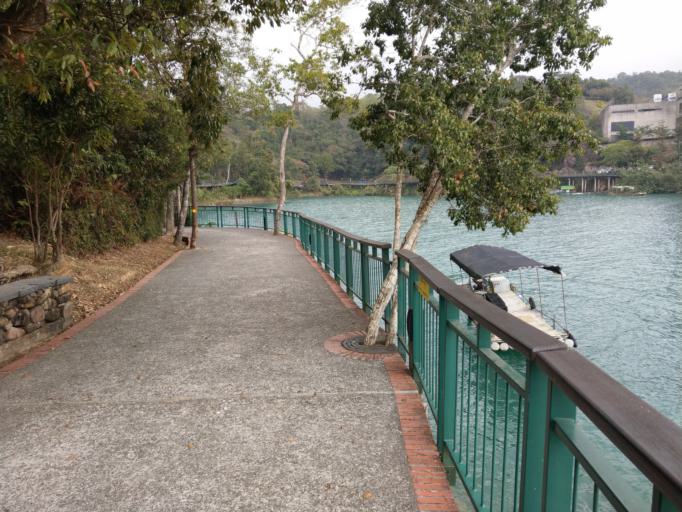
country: TW
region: Taiwan
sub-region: Nantou
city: Puli
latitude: 23.8713
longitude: 120.9212
